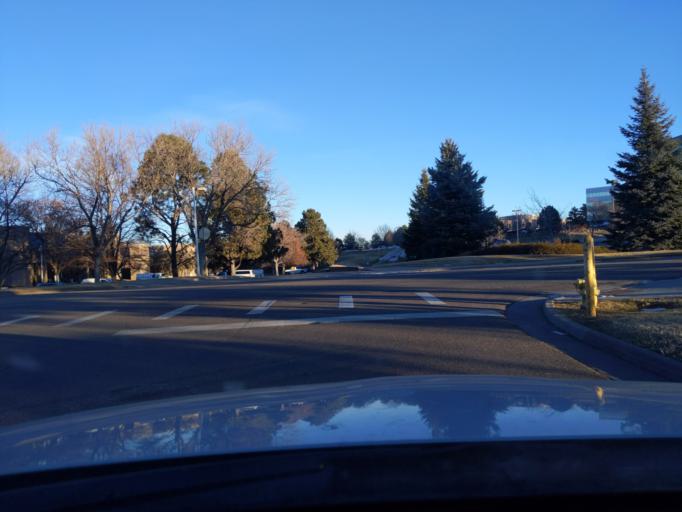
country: US
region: Colorado
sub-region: Arapahoe County
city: Centennial
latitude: 39.5718
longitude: -104.8836
